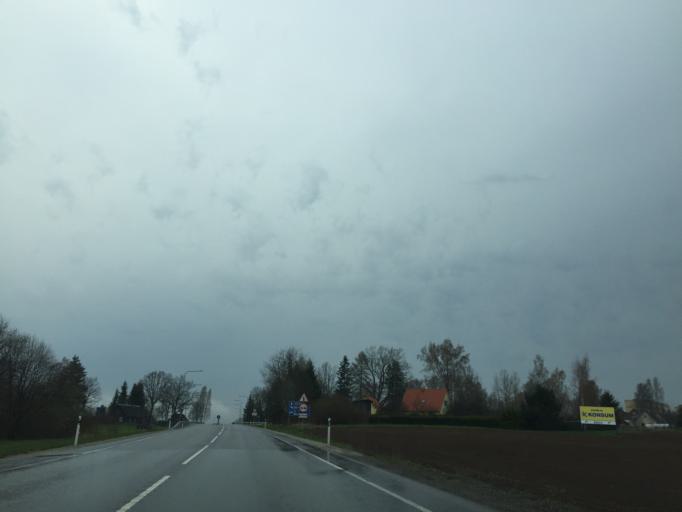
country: EE
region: Tartu
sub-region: UElenurme vald
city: Ulenurme
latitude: 58.2280
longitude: 26.6984
